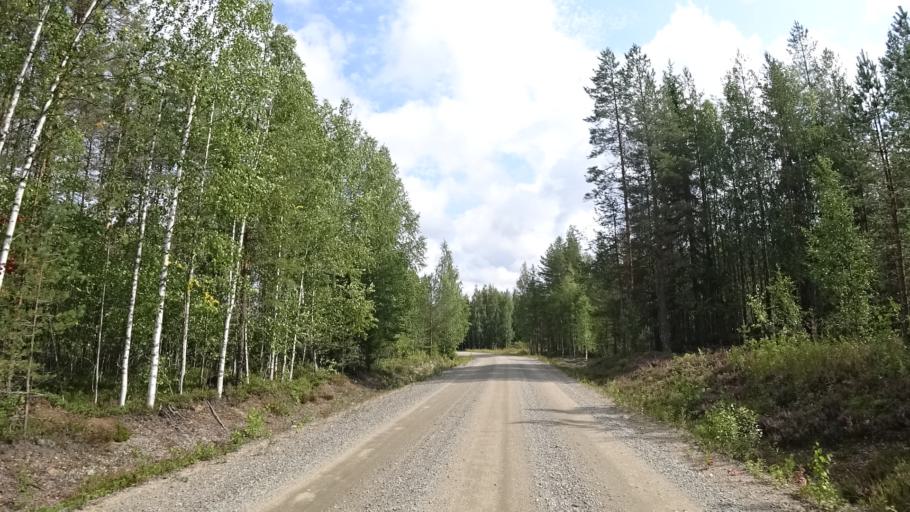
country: FI
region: North Karelia
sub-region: Joensuu
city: Ilomantsi
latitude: 62.9264
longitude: 31.3876
